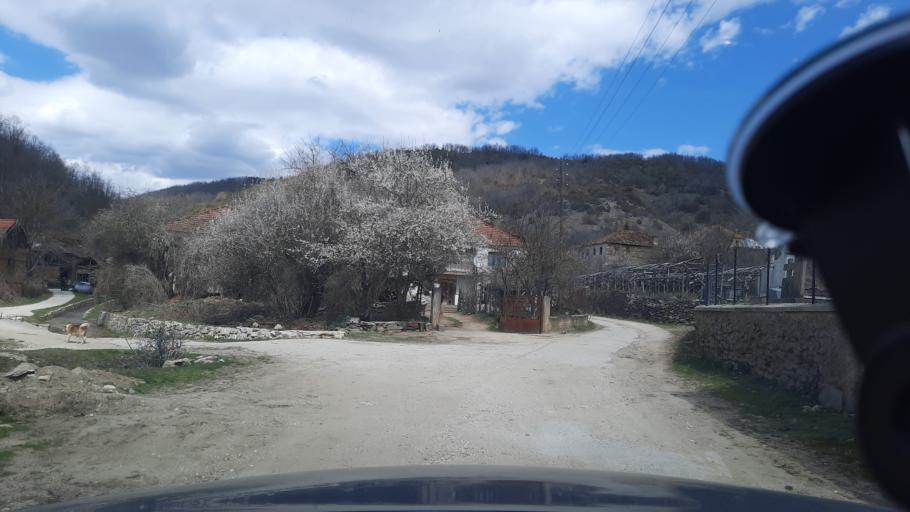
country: MK
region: Demir Hisar
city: Sopotnica
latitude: 41.2997
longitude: 21.1524
